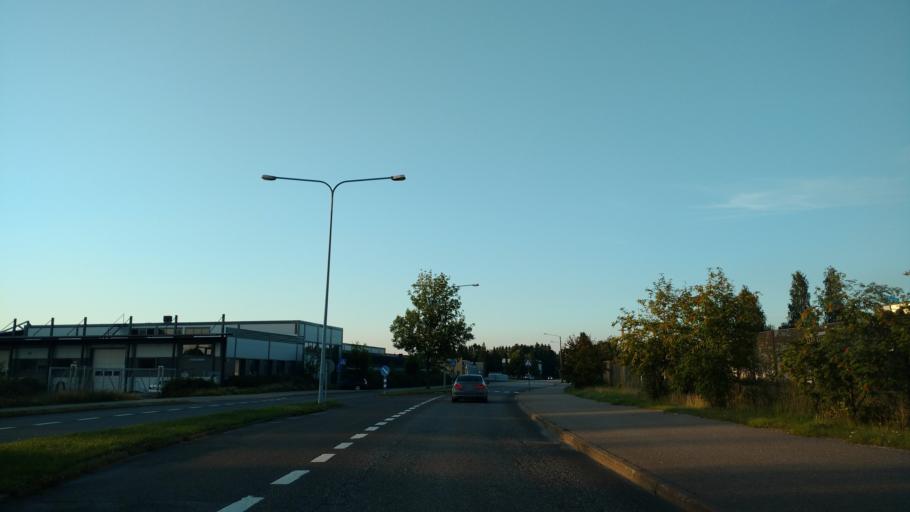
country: FI
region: Varsinais-Suomi
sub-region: Salo
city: Salo
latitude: 60.3759
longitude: 23.1164
